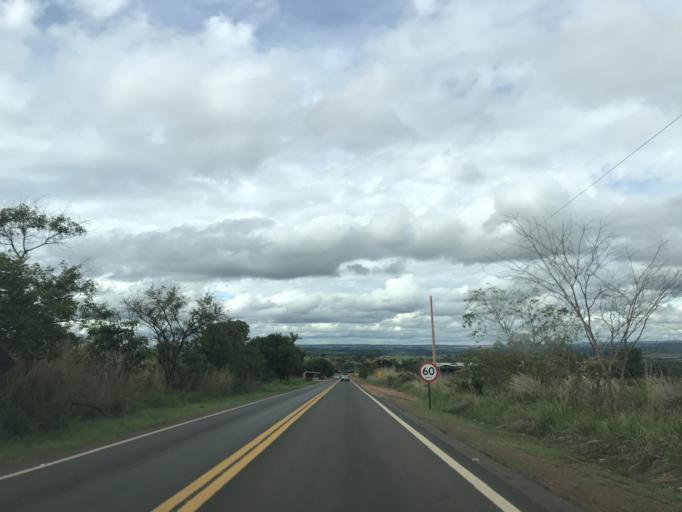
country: BR
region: Goias
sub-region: Piracanjuba
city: Piracanjuba
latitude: -17.2067
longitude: -48.7059
